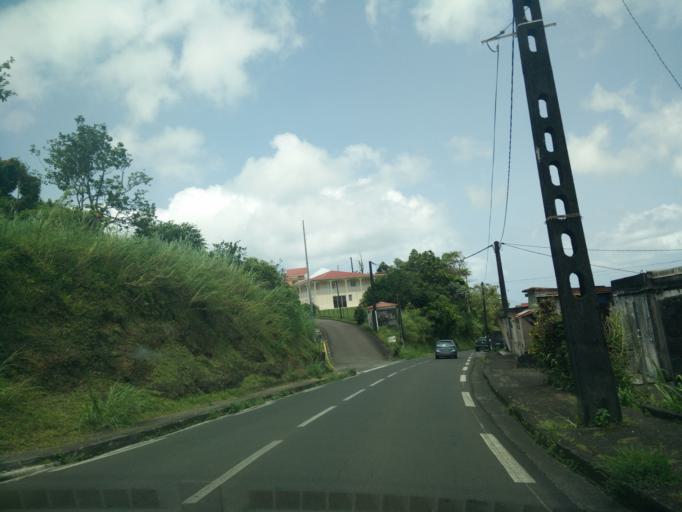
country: MQ
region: Martinique
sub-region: Martinique
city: Le Morne-Rouge
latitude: 14.7708
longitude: -61.1384
